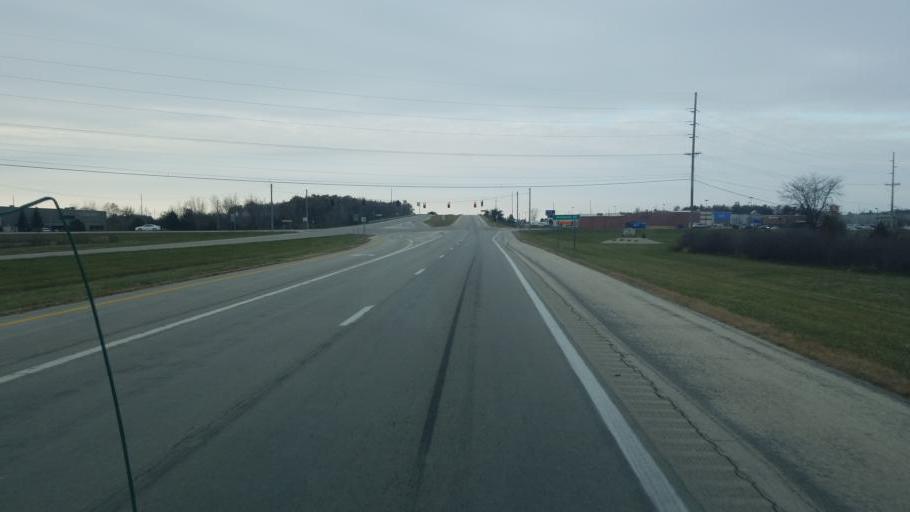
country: US
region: Ohio
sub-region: Mercer County
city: Celina
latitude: 40.5576
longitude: -84.5345
